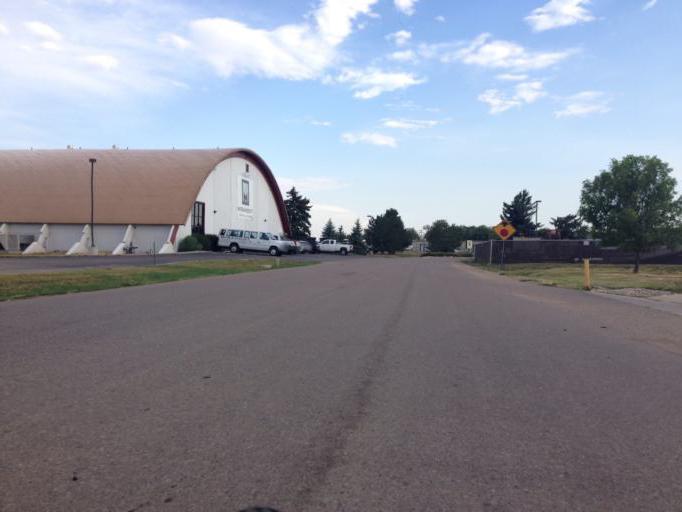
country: US
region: Colorado
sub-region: Larimer County
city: Fort Collins
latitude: 40.5867
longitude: -105.0443
